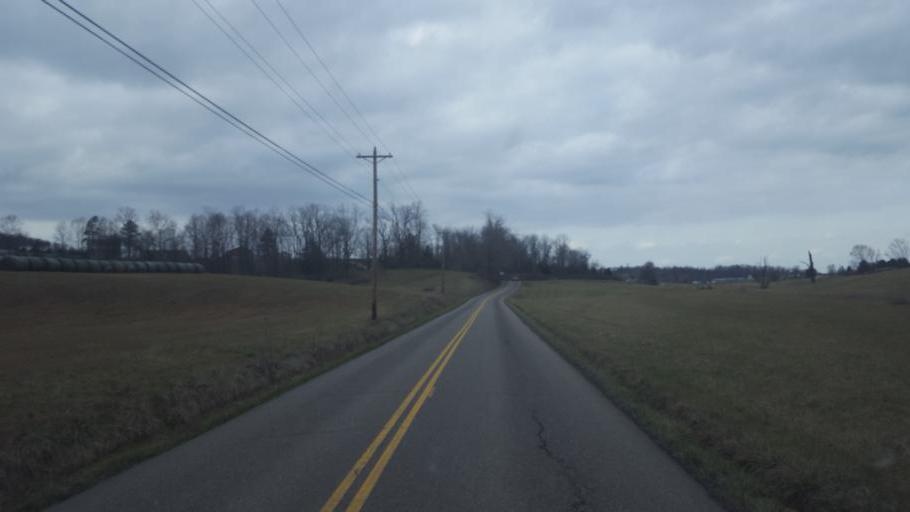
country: US
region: Ohio
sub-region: Gallia County
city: Gallipolis
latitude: 38.7668
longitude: -82.3758
